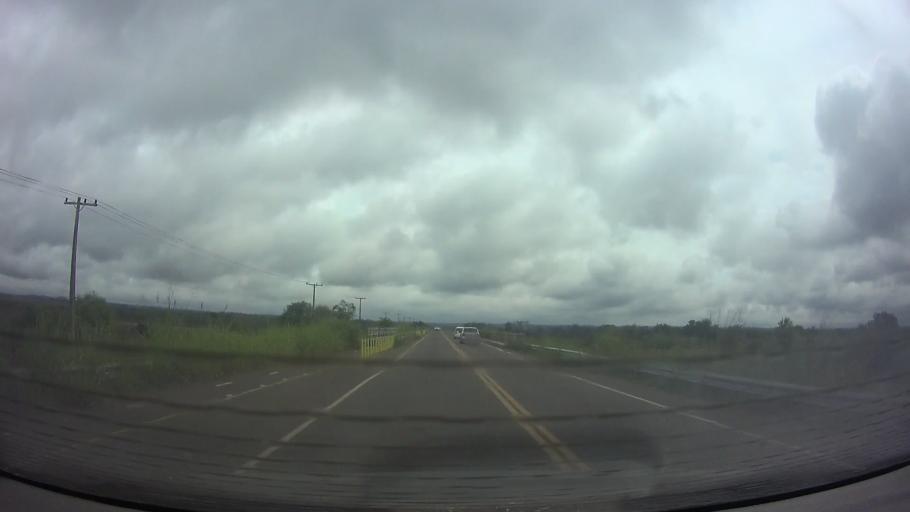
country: PY
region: Cordillera
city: Emboscada
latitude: -25.2045
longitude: -57.3696
